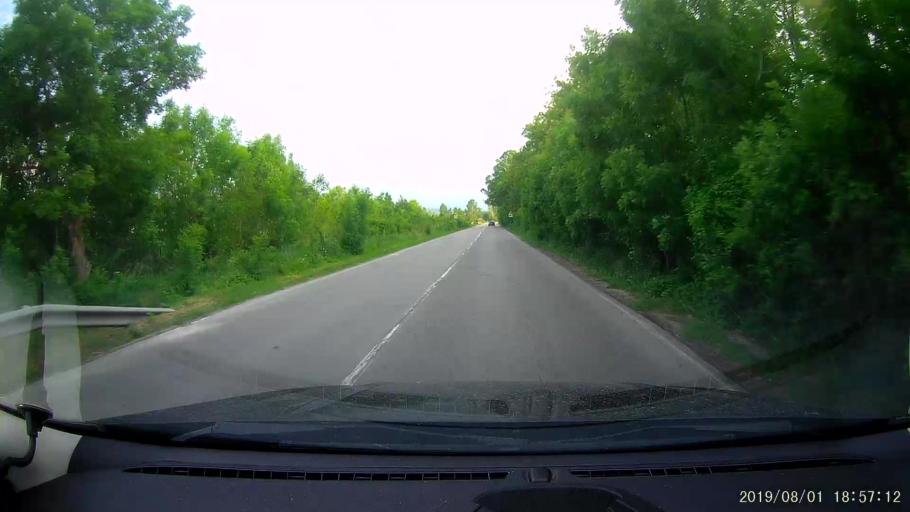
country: BG
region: Shumen
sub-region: Obshtina Smyadovo
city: Smyadovo
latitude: 43.1512
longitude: 27.0215
